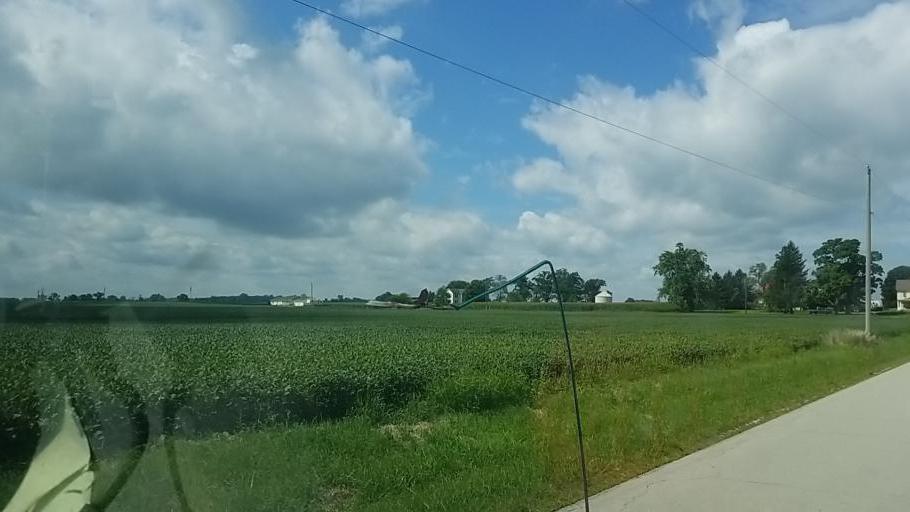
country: US
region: Ohio
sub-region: Fayette County
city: Jeffersonville
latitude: 39.6855
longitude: -83.5013
